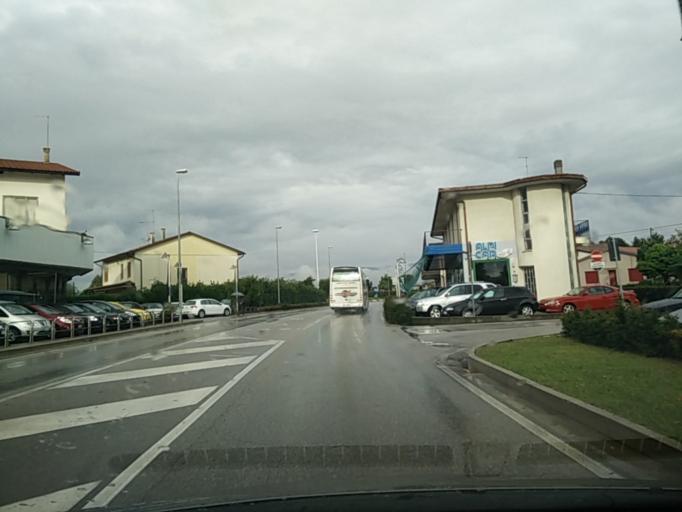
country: IT
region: Veneto
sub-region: Provincia di Vicenza
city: Rossano Veneto
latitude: 45.7084
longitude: 11.8013
